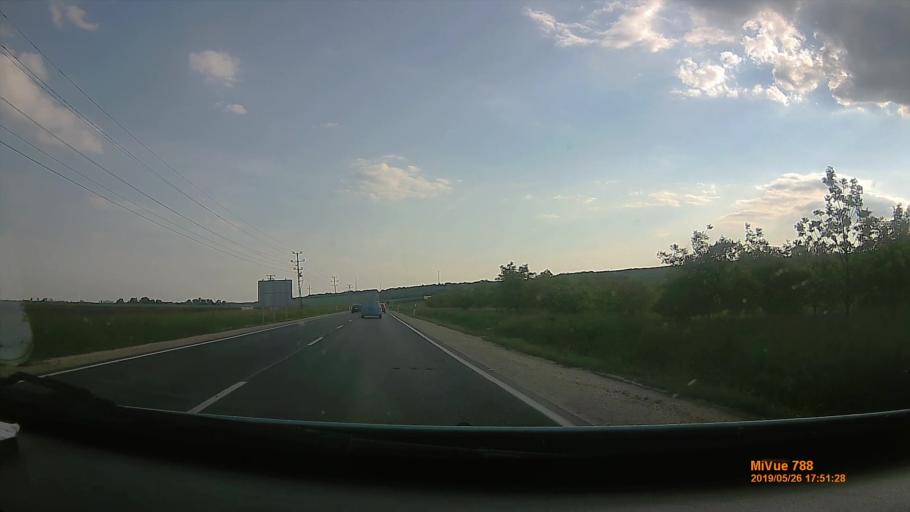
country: HU
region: Borsod-Abauj-Zemplen
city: Szikszo
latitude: 48.1745
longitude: 20.9139
